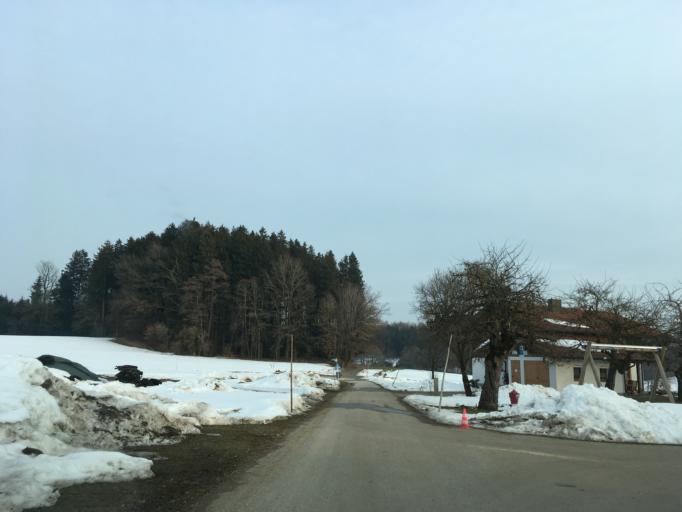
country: DE
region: Bavaria
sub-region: Upper Bavaria
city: Bad Endorf
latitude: 47.9255
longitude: 12.2996
